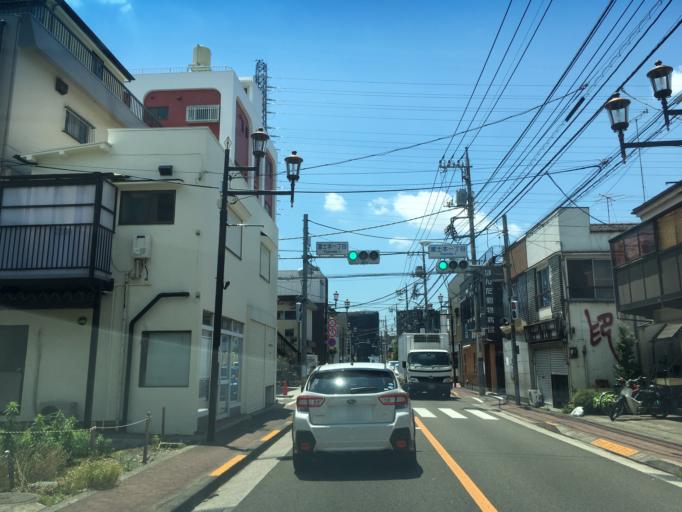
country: JP
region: Tokyo
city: Kokubunji
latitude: 35.7021
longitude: 139.4508
